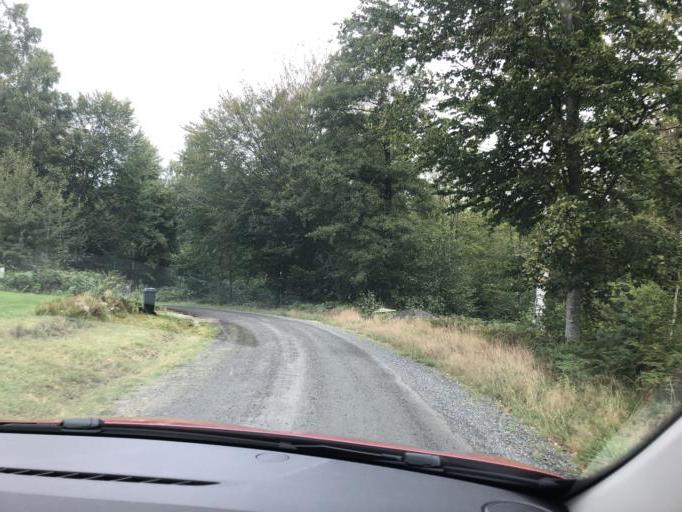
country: SE
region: Blekinge
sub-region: Solvesborgs Kommun
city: Soelvesborg
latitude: 56.1387
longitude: 14.5855
